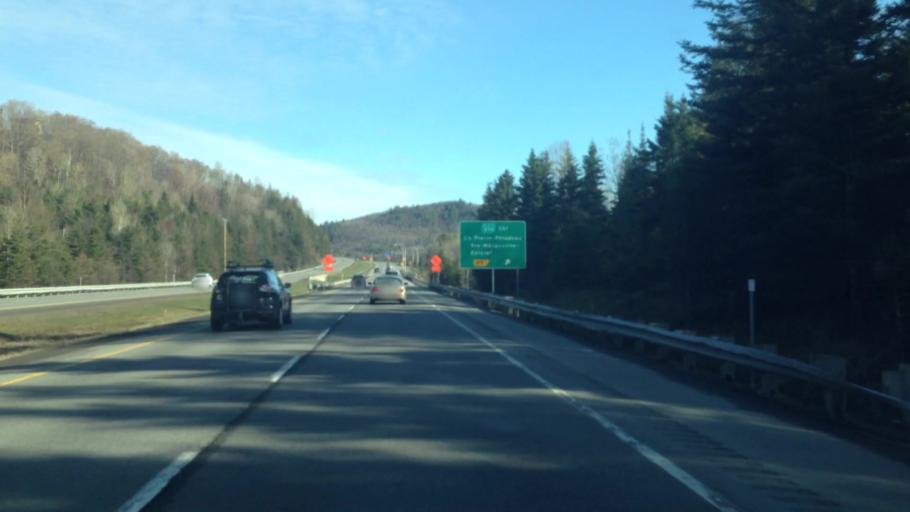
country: CA
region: Quebec
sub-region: Laurentides
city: Sainte-Adele
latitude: 45.9509
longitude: -74.1260
